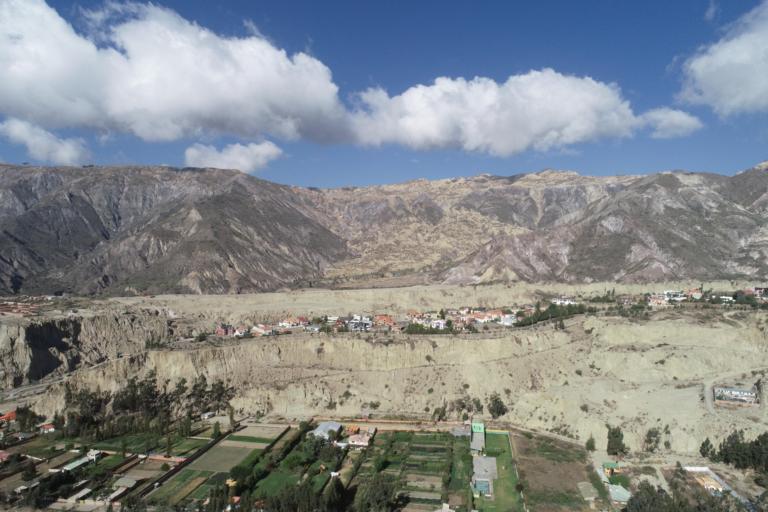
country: BO
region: La Paz
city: La Paz
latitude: -16.6114
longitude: -68.0630
